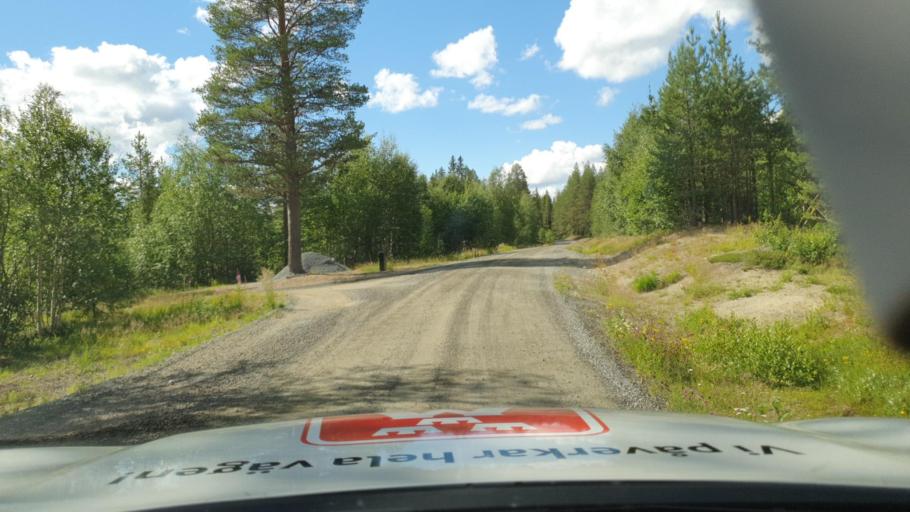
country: SE
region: Vaesterbotten
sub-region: Sorsele Kommun
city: Sorsele
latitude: 65.4125
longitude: 17.5250
